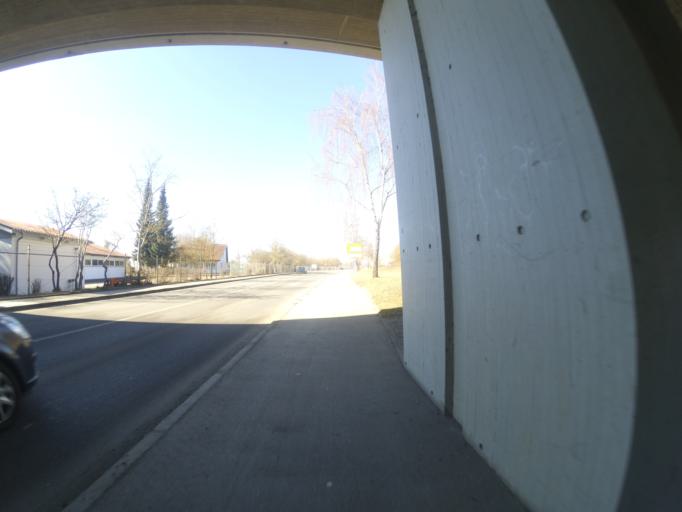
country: DE
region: Baden-Wuerttemberg
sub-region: Tuebingen Region
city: Laupheim
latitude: 48.2283
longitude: 9.8673
